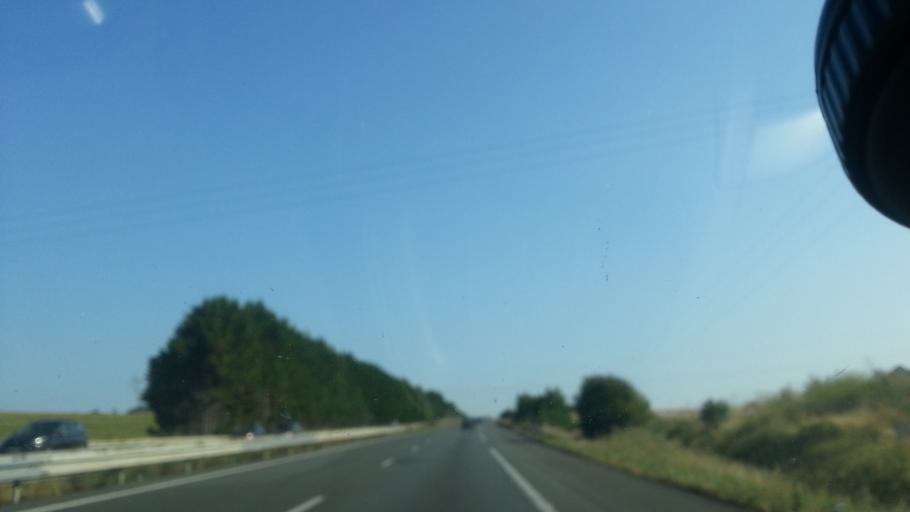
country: FR
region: Poitou-Charentes
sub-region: Departement de la Vienne
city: Antran
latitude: 46.8860
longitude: 0.5180
